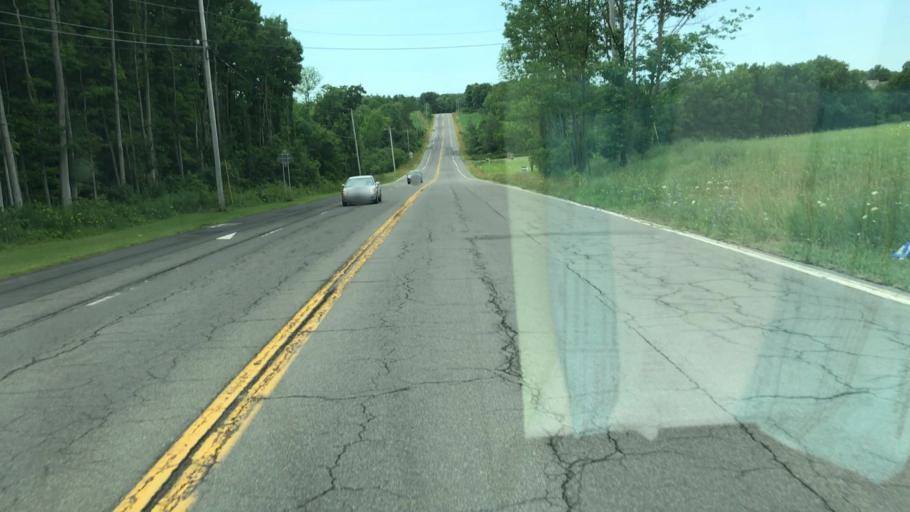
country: US
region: New York
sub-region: Onondaga County
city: Skaneateles
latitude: 42.9393
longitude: -76.3771
